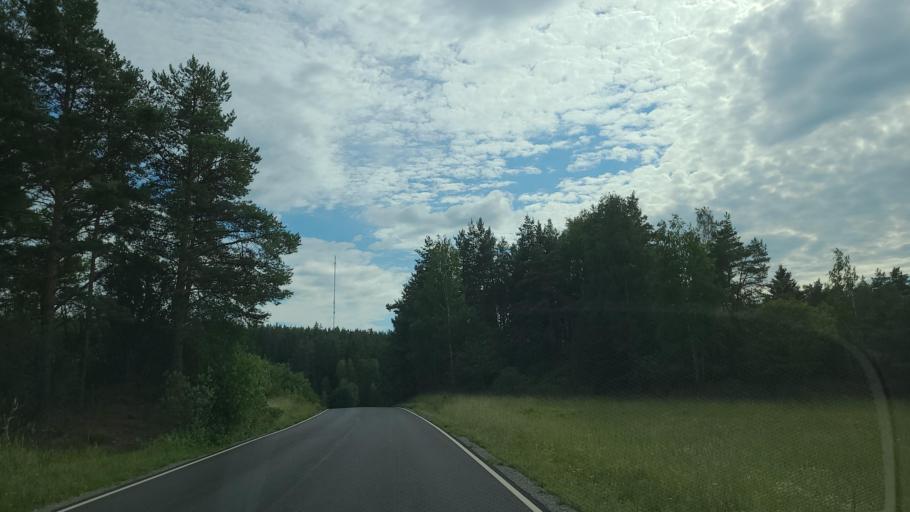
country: FI
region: Varsinais-Suomi
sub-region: Turku
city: Rymaettylae
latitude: 60.3284
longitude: 21.9708
